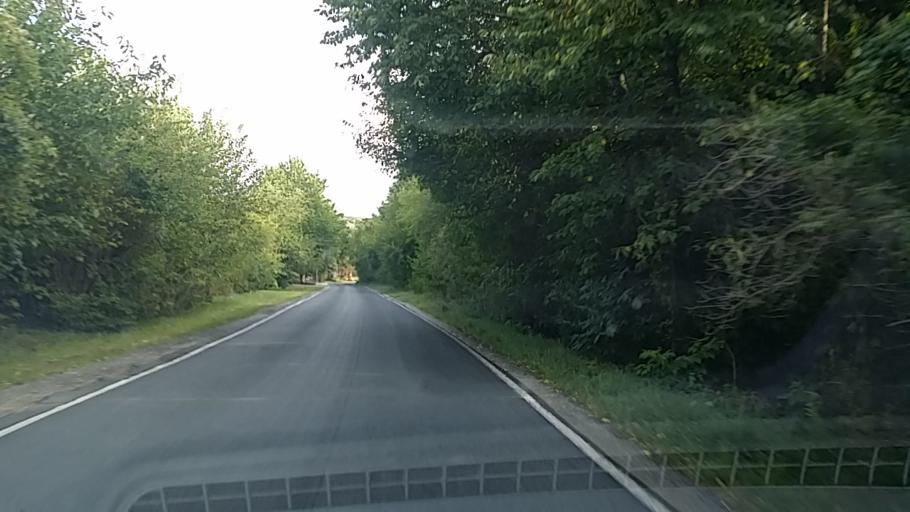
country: HU
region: Gyor-Moson-Sopron
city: Fertorakos
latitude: 47.7284
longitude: 16.6225
